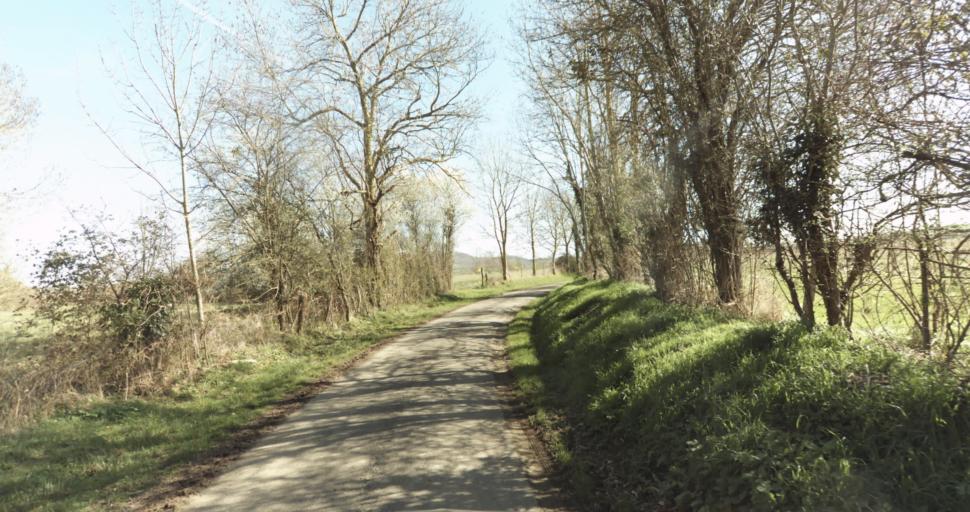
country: FR
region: Lower Normandy
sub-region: Departement du Calvados
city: Saint-Pierre-sur-Dives
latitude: 49.0318
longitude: 0.0197
